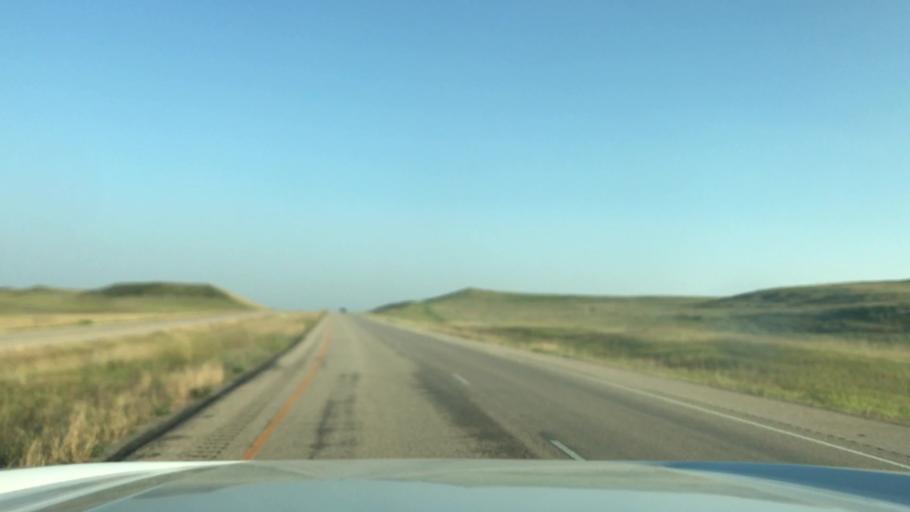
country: US
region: Montana
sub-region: Big Horn County
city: Crow Agency
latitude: 45.2302
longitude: -107.3641
